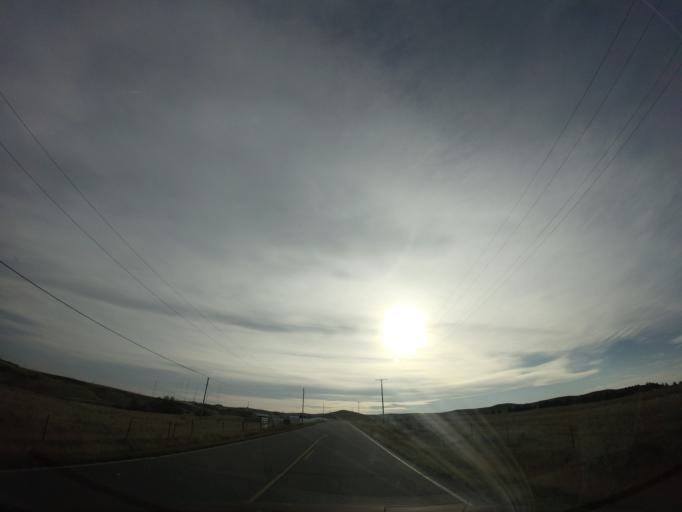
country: US
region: Montana
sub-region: Yellowstone County
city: Billings
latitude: 45.7823
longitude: -108.4603
